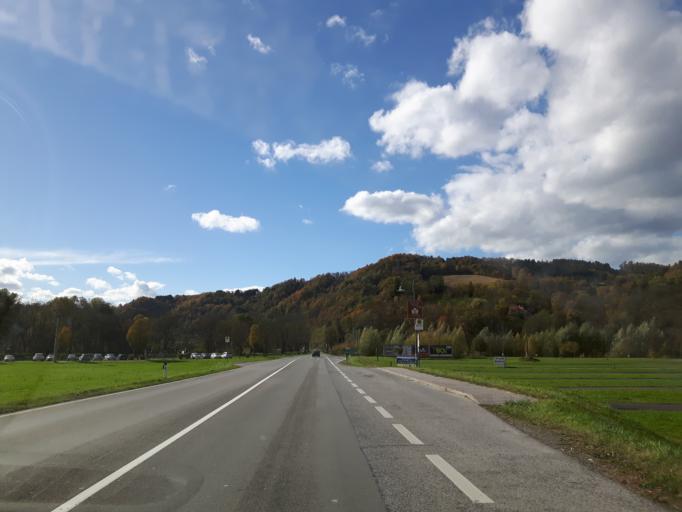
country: AT
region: Styria
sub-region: Politischer Bezirk Leibnitz
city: Kaindorf an der Sulm
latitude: 46.7944
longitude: 15.5298
